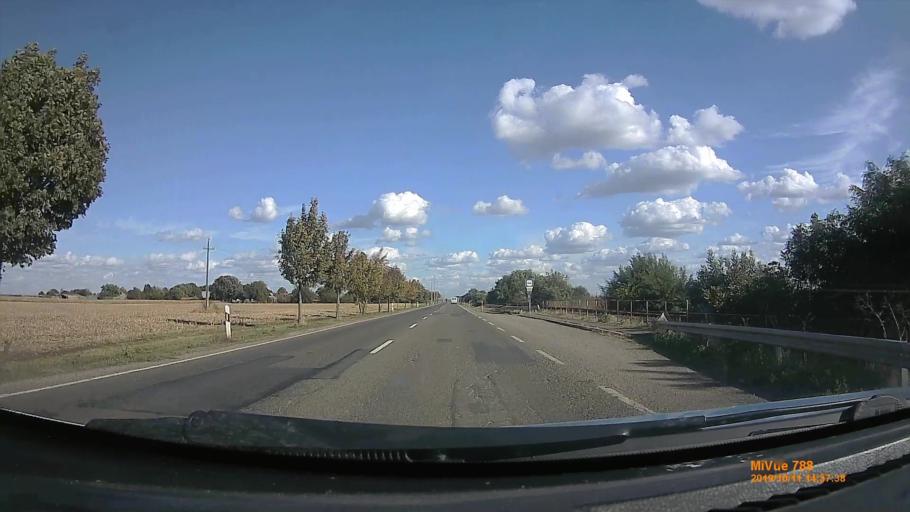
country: HU
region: Hajdu-Bihar
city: Ebes
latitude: 47.5531
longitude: 21.5300
